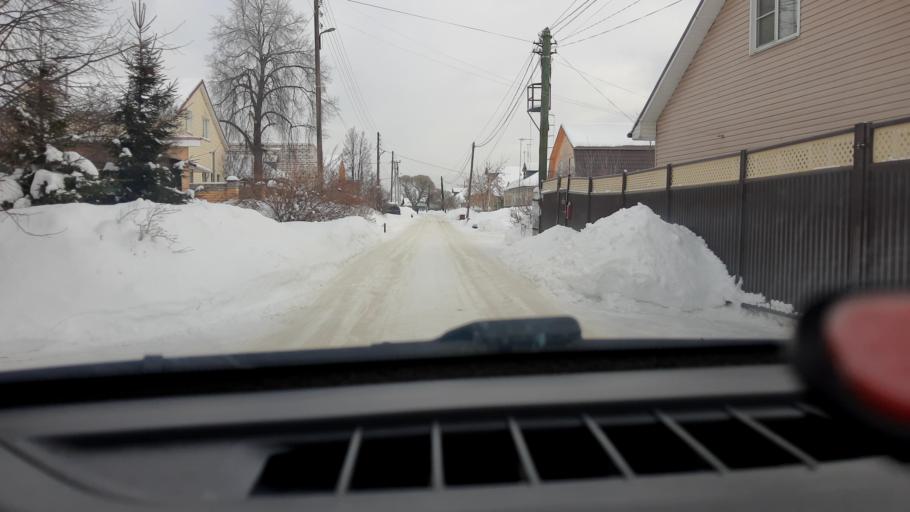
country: RU
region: Nizjnij Novgorod
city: Gorbatovka
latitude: 56.2584
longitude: 43.7358
